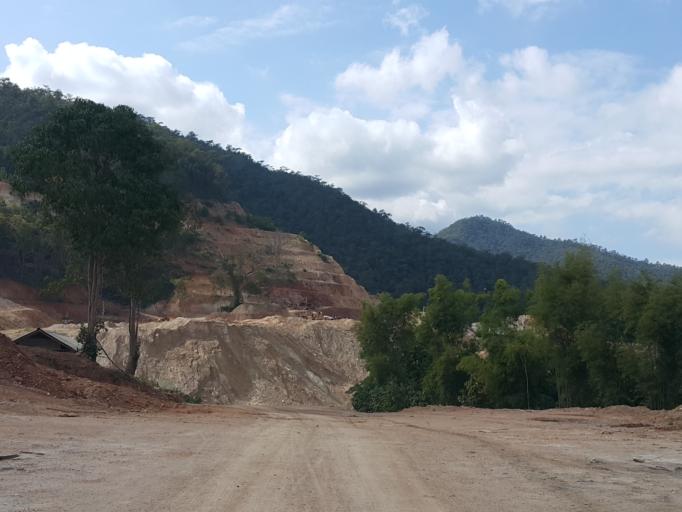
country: TH
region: Lampang
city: Chae Hom
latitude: 18.5715
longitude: 99.4406
